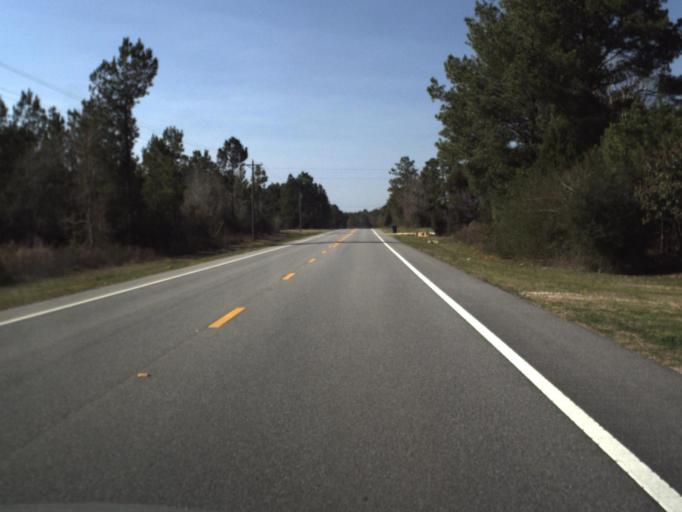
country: US
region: Florida
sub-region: Gulf County
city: Wewahitchka
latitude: 30.2443
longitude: -85.2219
